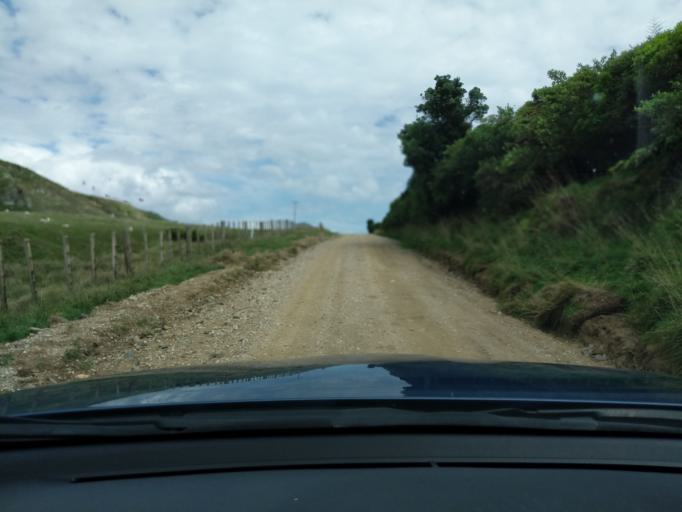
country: NZ
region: Tasman
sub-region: Tasman District
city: Takaka
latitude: -40.6474
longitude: 172.4286
